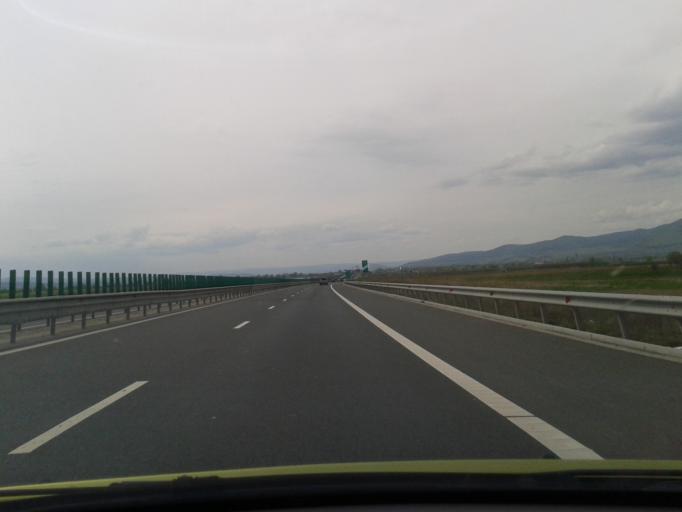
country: RO
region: Hunedoara
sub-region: Comuna Romos
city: Romos
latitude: 45.8931
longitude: 23.2767
